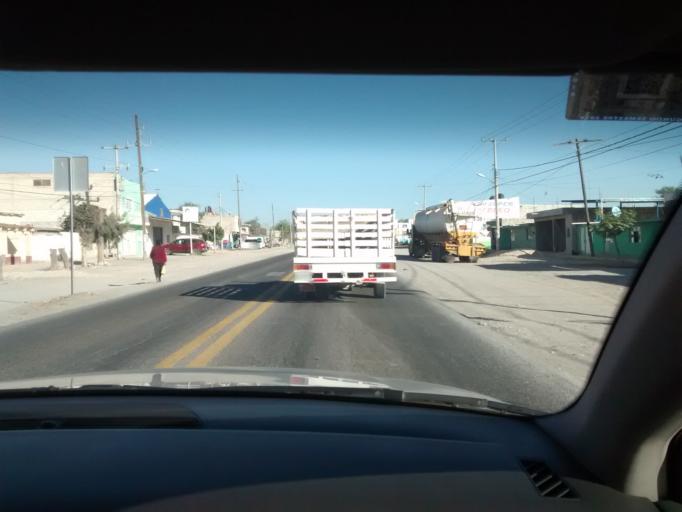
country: MX
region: Puebla
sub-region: Santiago Miahuatlan
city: San Jose Monte Chiquito
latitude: 18.4931
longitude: -97.4655
